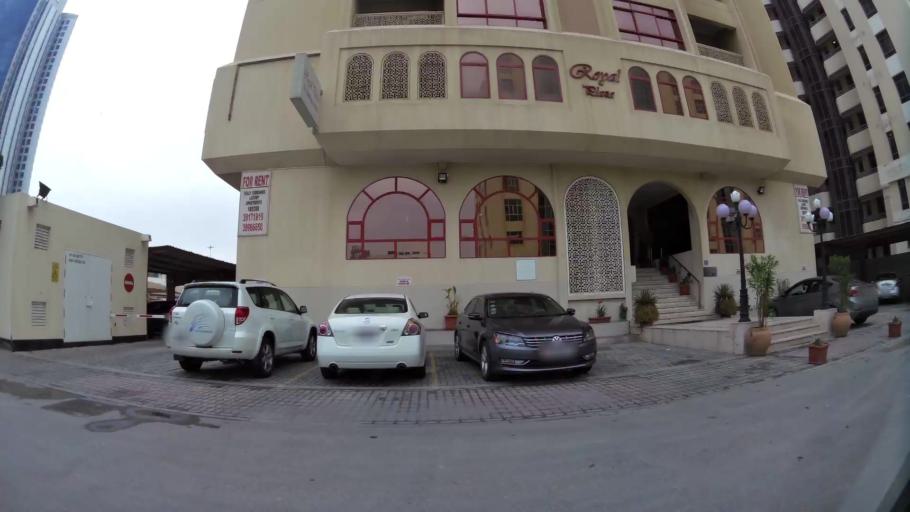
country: BH
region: Manama
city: Manama
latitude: 26.2390
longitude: 50.5921
